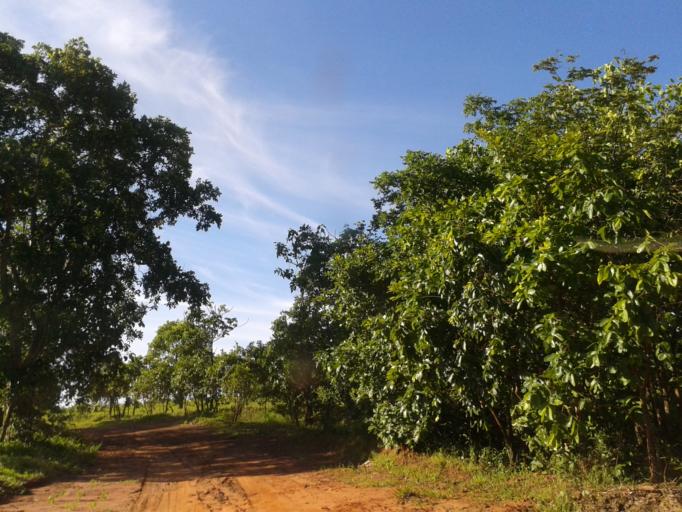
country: BR
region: Minas Gerais
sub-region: Santa Vitoria
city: Santa Vitoria
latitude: -19.0962
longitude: -49.9704
